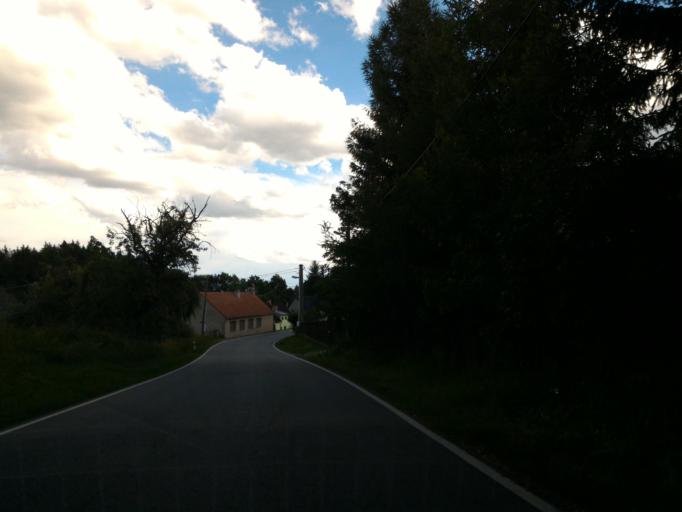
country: CZ
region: Vysocina
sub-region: Okres Jihlava
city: Telc
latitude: 49.2231
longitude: 15.4226
